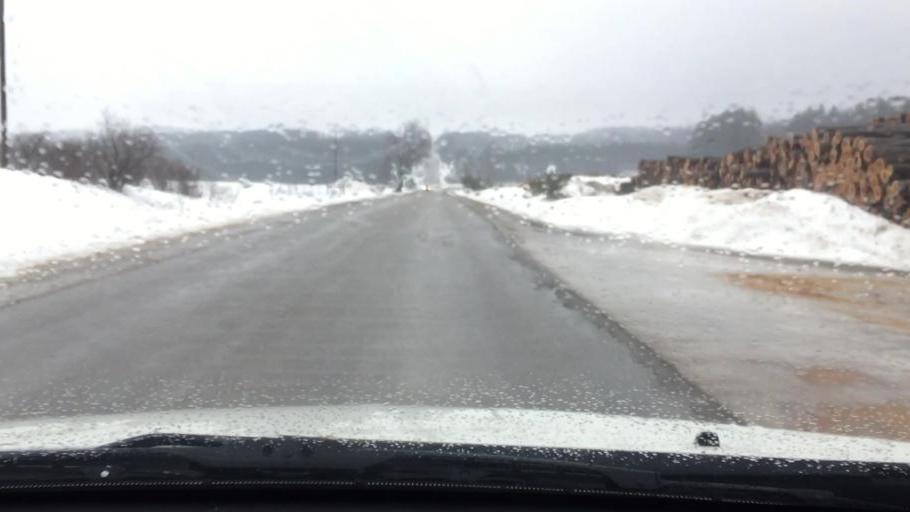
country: US
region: Michigan
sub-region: Charlevoix County
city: East Jordan
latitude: 45.1022
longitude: -85.1600
